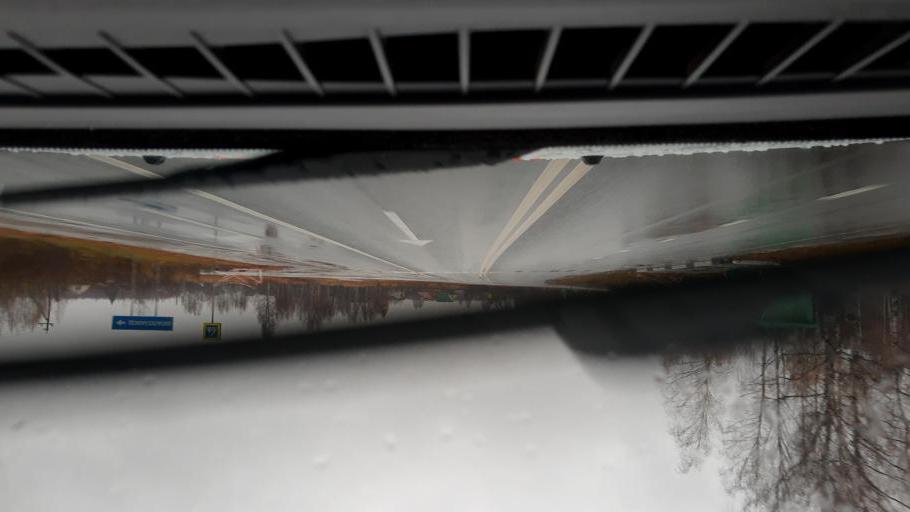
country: RU
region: Nizjnij Novgorod
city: Sitniki
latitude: 56.5240
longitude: 44.0263
